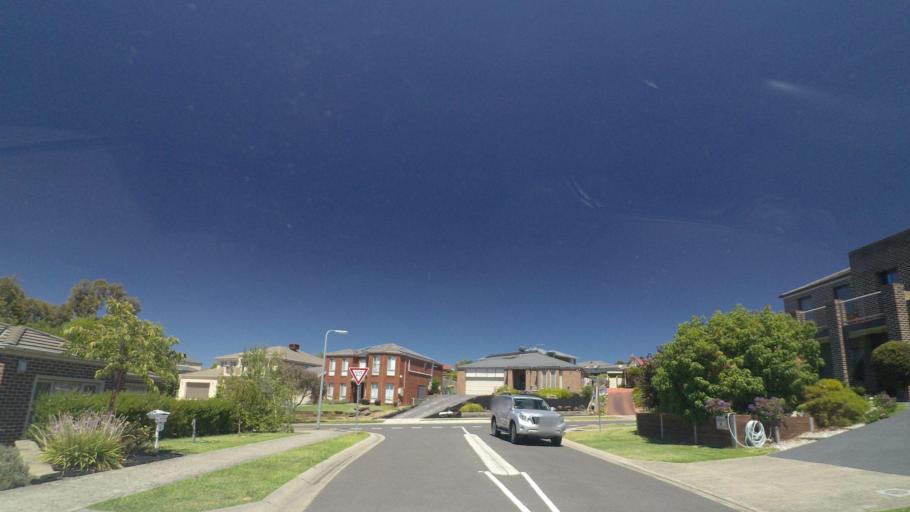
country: AU
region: Victoria
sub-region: Yarra Ranges
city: Lilydale
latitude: -37.7389
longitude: 145.3406
